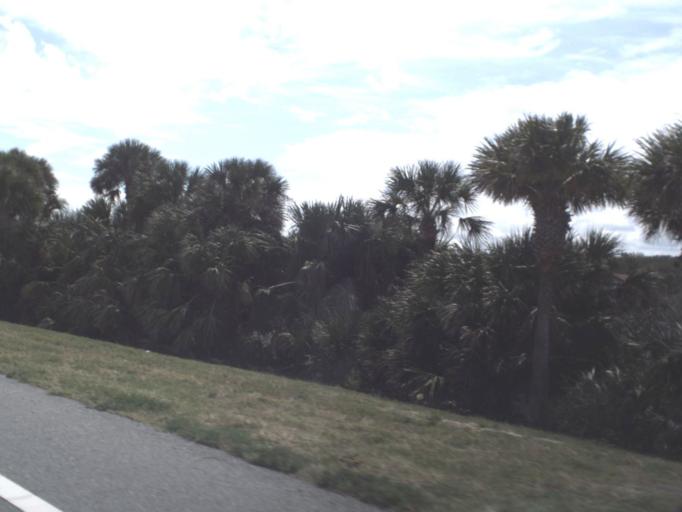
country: US
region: Florida
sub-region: Flagler County
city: Palm Coast
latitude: 29.6492
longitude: -81.2075
